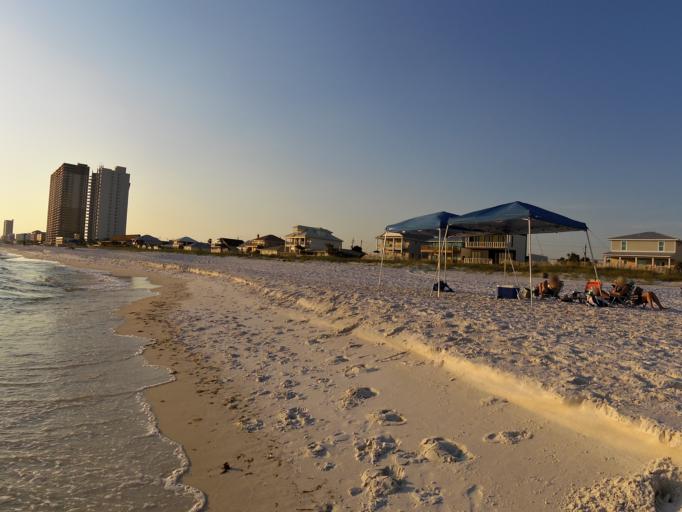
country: US
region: Florida
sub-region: Bay County
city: Laguna Beach
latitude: 30.2165
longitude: -85.8808
